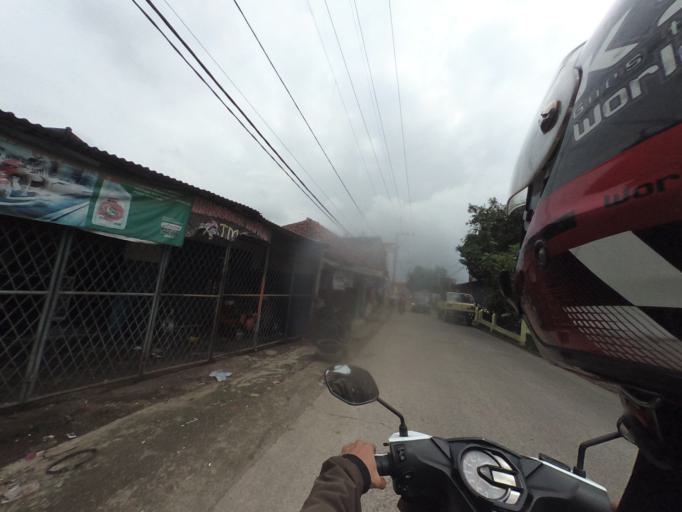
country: ID
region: West Java
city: Bogor
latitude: -6.6040
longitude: 106.7589
